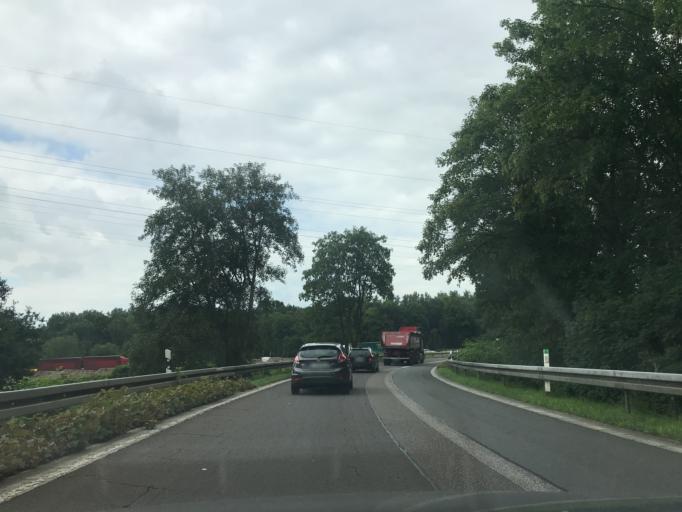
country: DE
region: North Rhine-Westphalia
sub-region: Regierungsbezirk Dusseldorf
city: Erkrath
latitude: 51.1884
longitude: 6.8719
